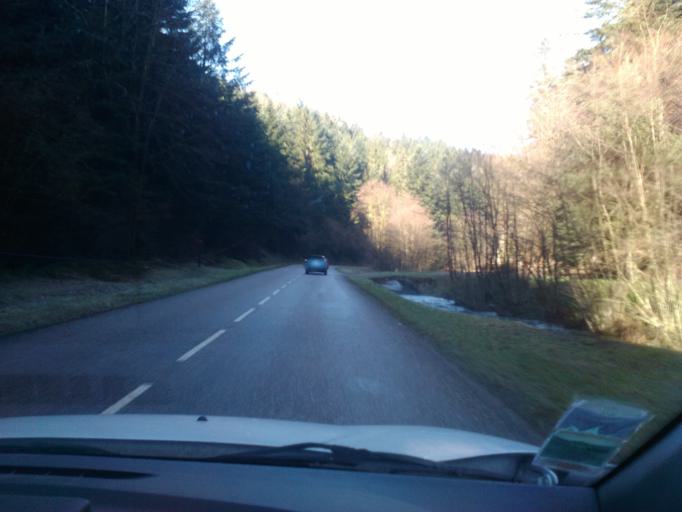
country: FR
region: Lorraine
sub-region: Departement des Vosges
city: Plombieres-les-Bains
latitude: 47.9588
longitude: 6.5249
